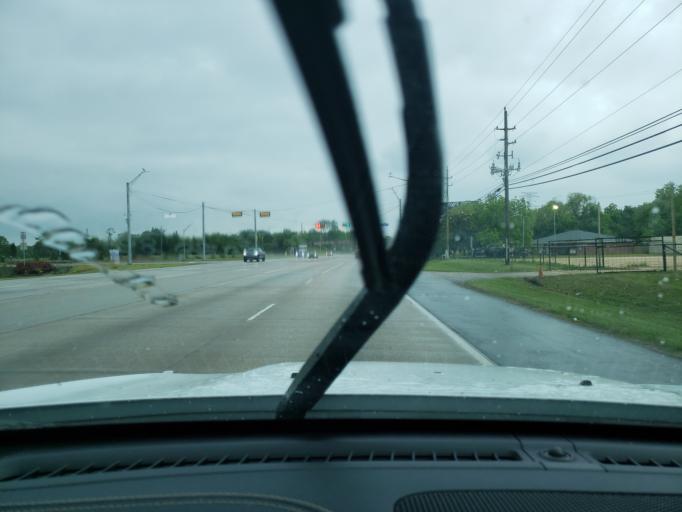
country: US
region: Texas
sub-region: Chambers County
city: Mont Belvieu
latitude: 29.8024
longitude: -94.9043
